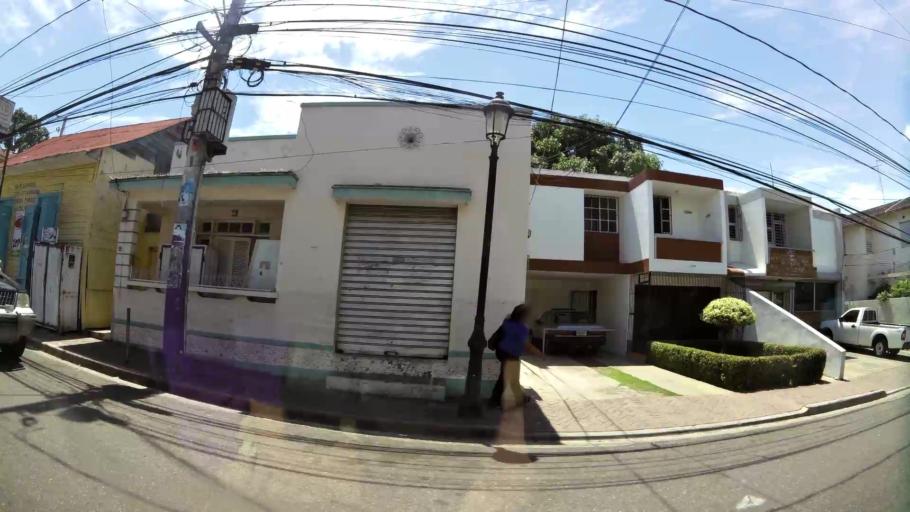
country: DO
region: Santiago
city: Santiago de los Caballeros
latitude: 19.4490
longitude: -70.6998
